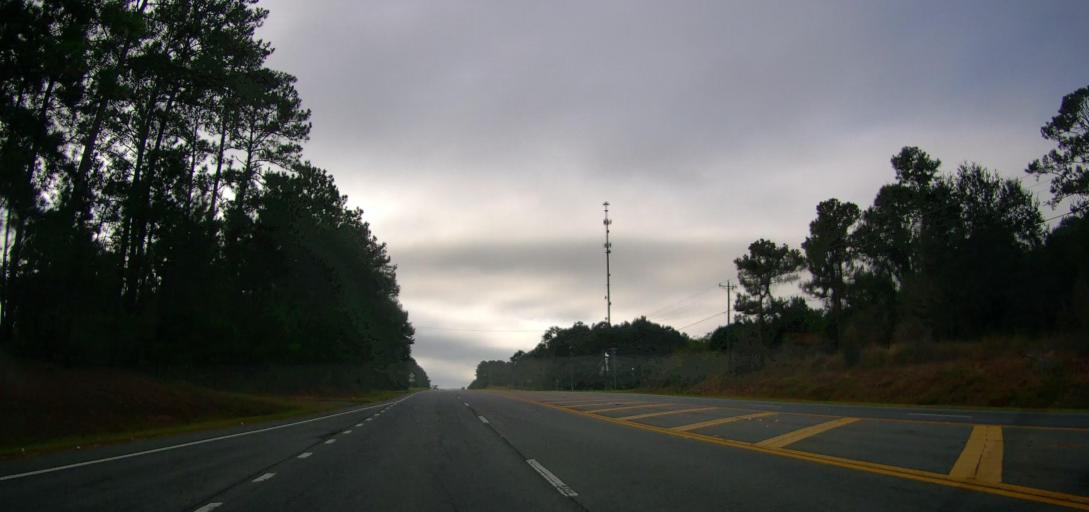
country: US
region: Georgia
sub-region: Tift County
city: Unionville
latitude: 31.3889
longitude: -83.5448
